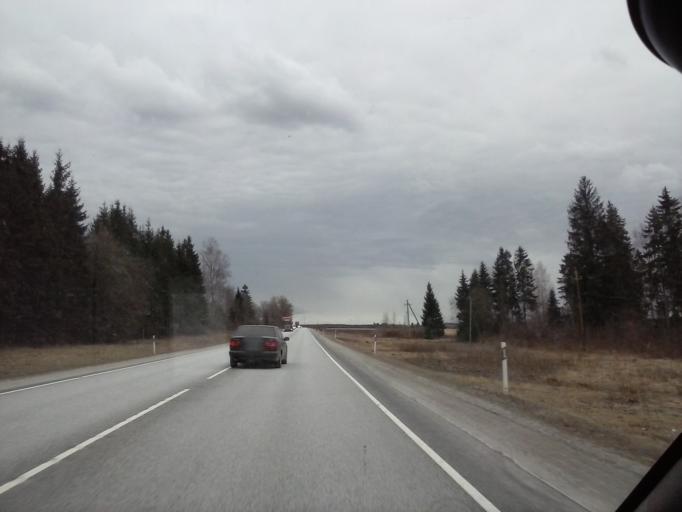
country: EE
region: Jaervamaa
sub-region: Paide linn
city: Paide
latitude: 59.0245
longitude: 25.5837
